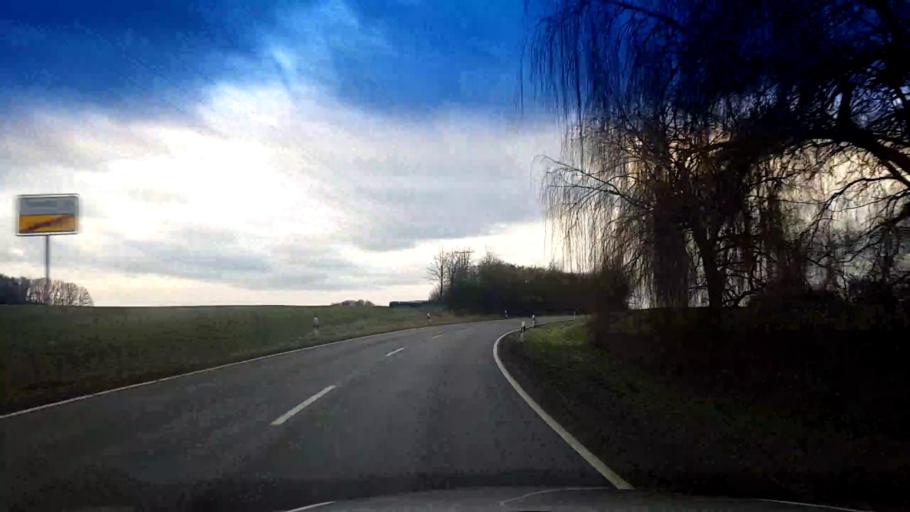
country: DE
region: Bavaria
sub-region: Upper Franconia
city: Litzendorf
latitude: 49.8664
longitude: 11.0254
